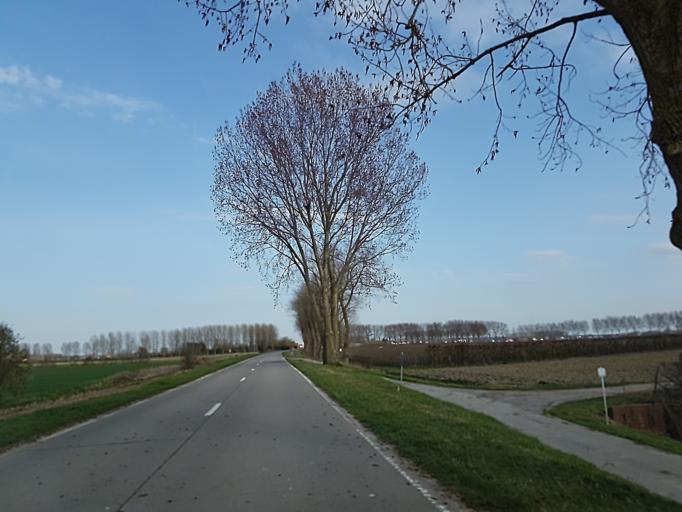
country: BE
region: Flanders
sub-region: Provincie Oost-Vlaanderen
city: Assenede
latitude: 51.2740
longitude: 3.7030
